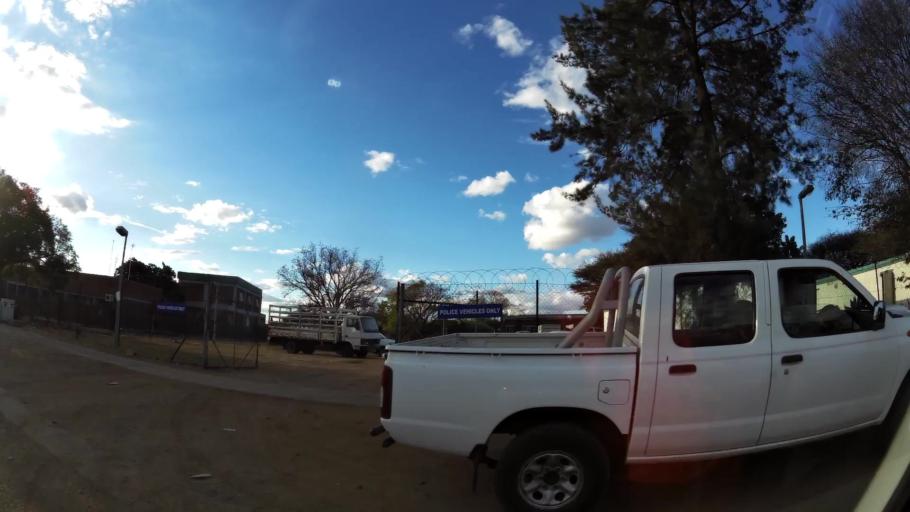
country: ZA
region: Limpopo
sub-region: Capricorn District Municipality
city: Polokwane
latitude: -23.9046
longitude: 29.4297
